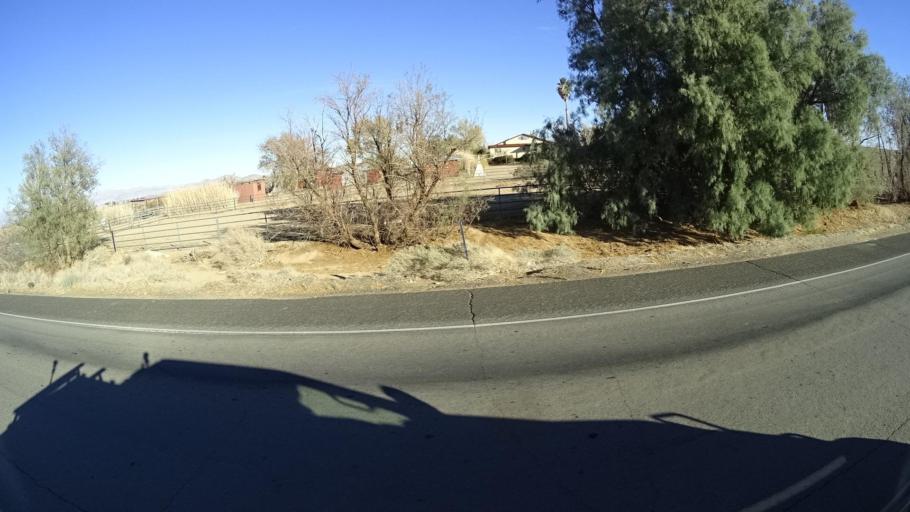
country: US
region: California
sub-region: Kern County
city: China Lake Acres
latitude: 35.6090
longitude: -117.7232
